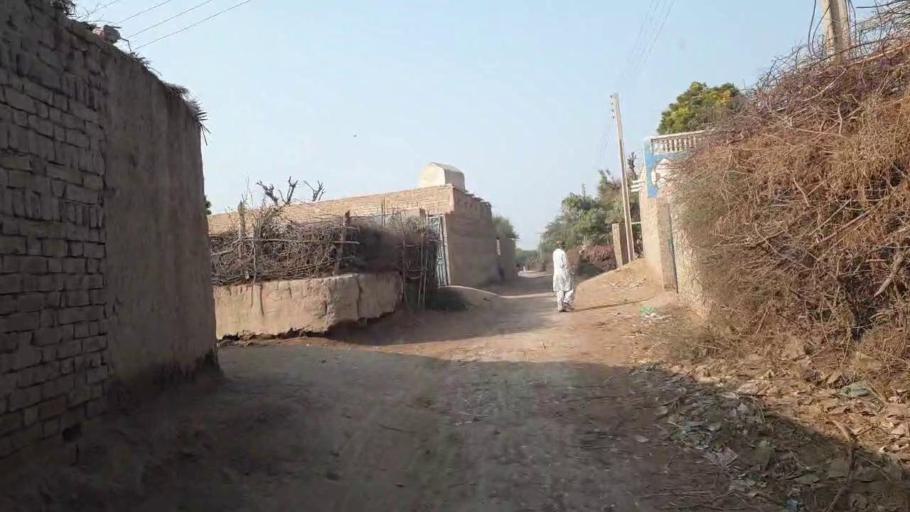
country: PK
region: Sindh
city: Bhit Shah
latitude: 25.8925
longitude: 68.4744
